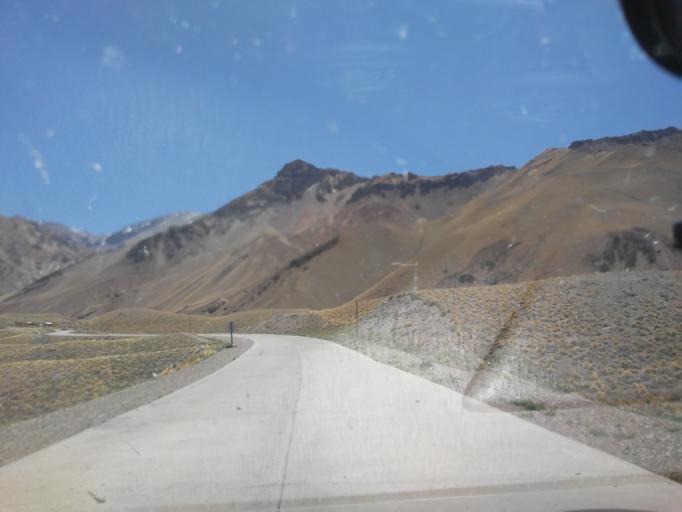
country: CL
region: Valparaiso
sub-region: Provincia de Los Andes
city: Los Andes
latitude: -32.8161
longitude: -69.9425
